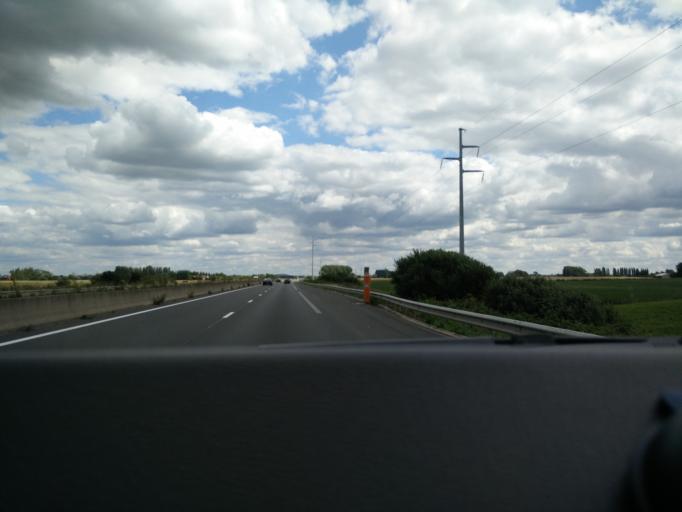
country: FR
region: Nord-Pas-de-Calais
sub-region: Departement du Nord
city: Wormhout
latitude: 50.8994
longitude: 2.4988
